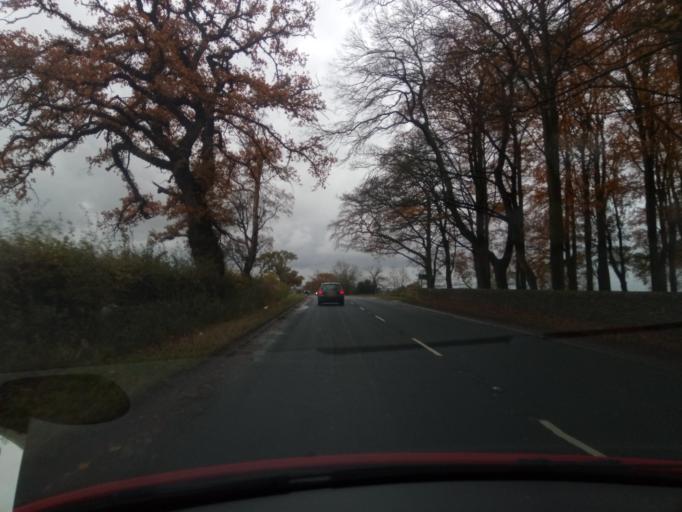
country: GB
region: England
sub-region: County Durham
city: Hamsterley
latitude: 54.7090
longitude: -1.7905
